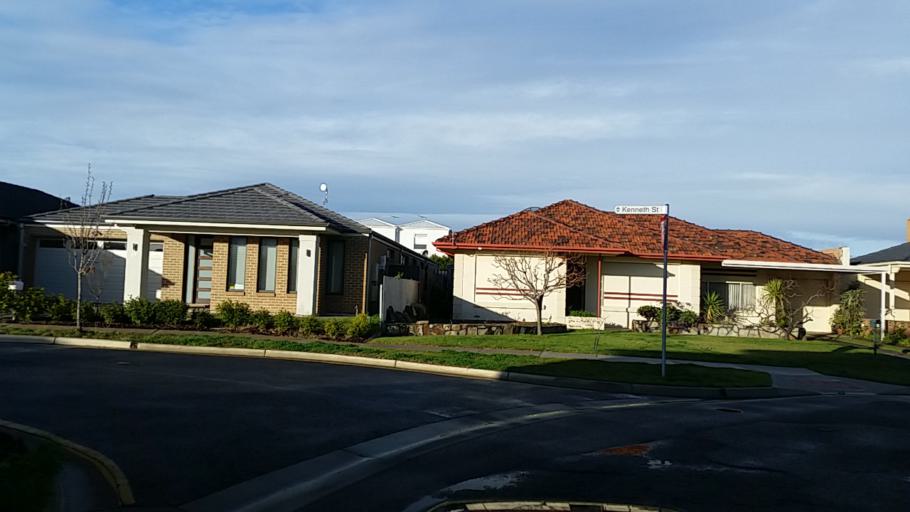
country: AU
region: South Australia
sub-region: Charles Sturt
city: Findon
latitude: -34.9033
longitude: 138.5360
